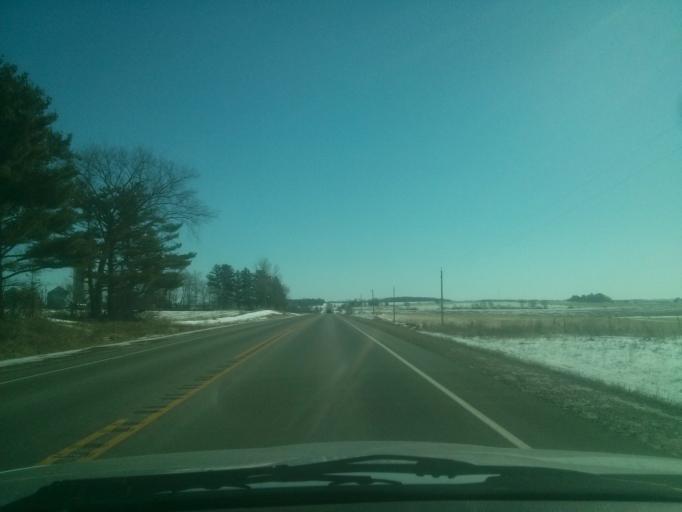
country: US
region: Wisconsin
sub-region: Polk County
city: Clear Lake
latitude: 45.1364
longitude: -92.3390
